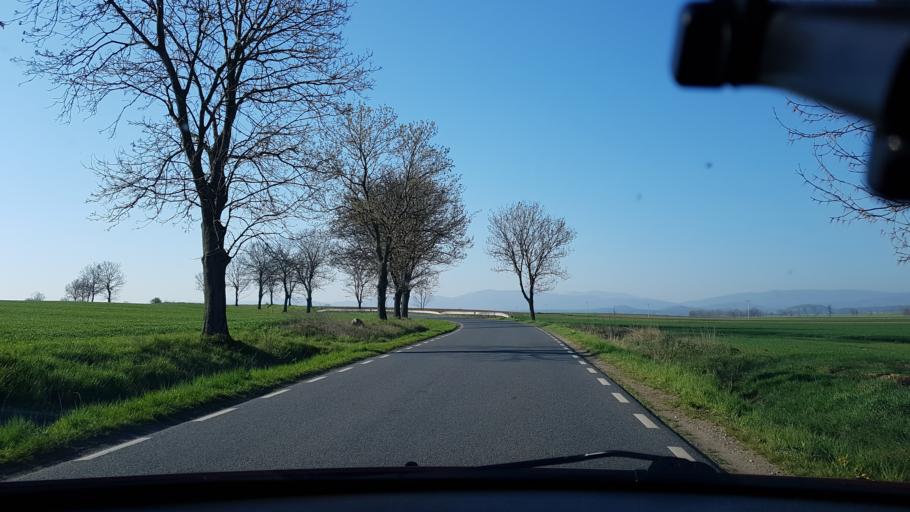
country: PL
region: Opole Voivodeship
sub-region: Powiat nyski
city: Otmuchow
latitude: 50.4202
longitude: 17.1801
